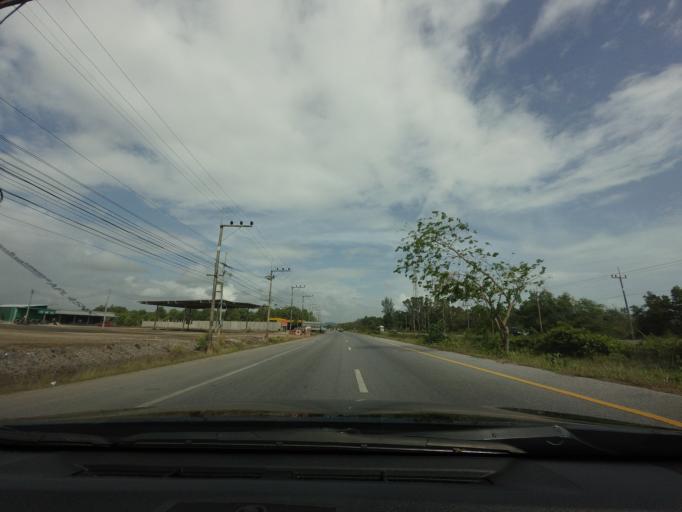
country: TH
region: Songkhla
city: Thepha
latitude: 6.8966
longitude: 100.9206
